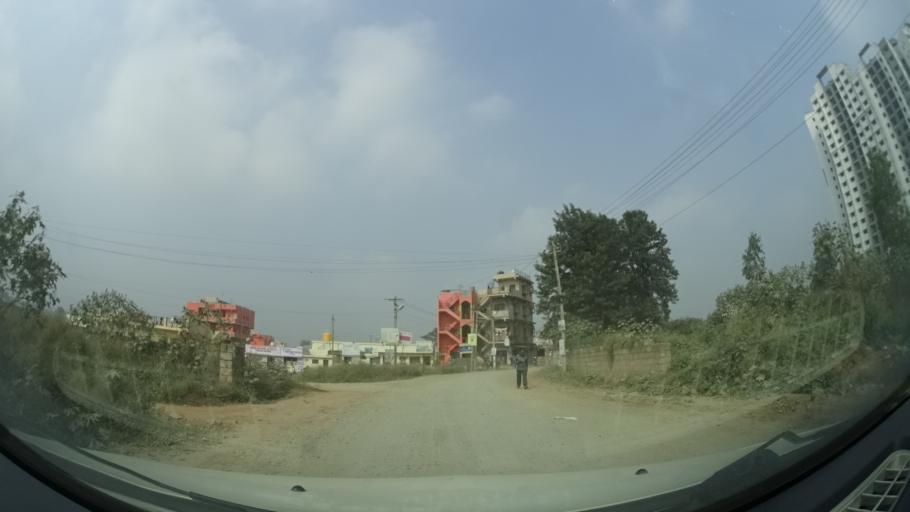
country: IN
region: Karnataka
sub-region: Bangalore Urban
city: Anekal
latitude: 12.8307
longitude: 77.6628
